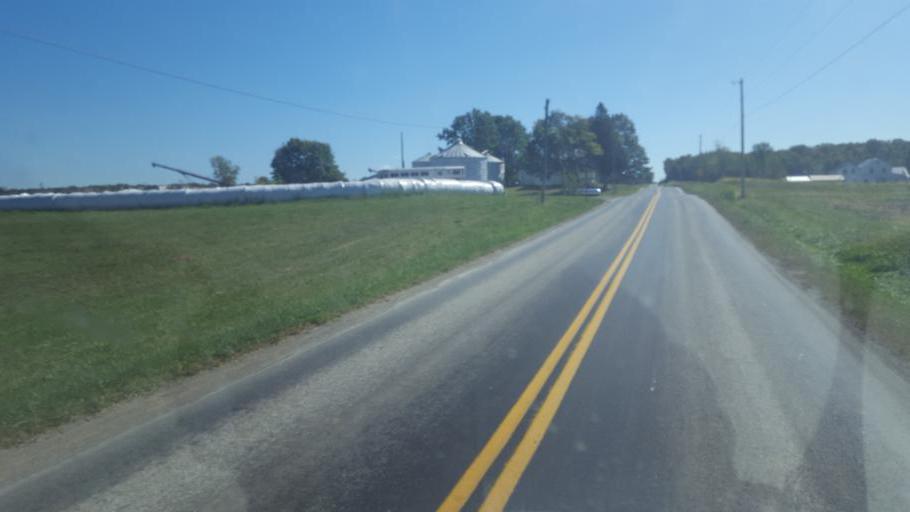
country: US
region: Ohio
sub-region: Wayne County
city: West Salem
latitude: 40.9734
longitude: -82.1629
